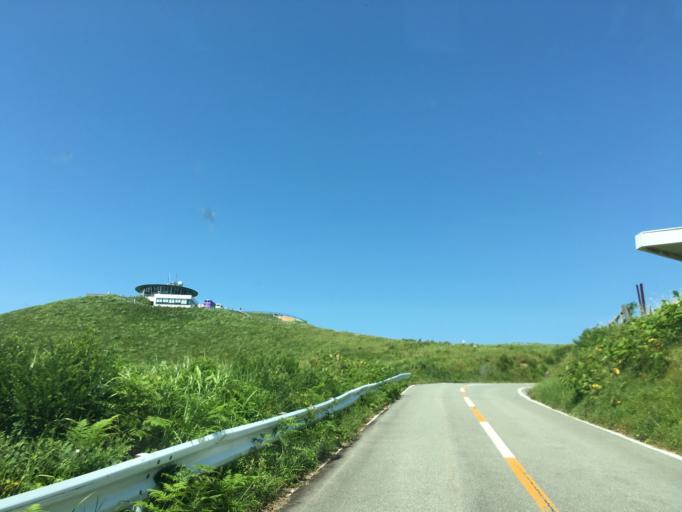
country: JP
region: Akita
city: Tenno
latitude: 39.9315
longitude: 139.8750
